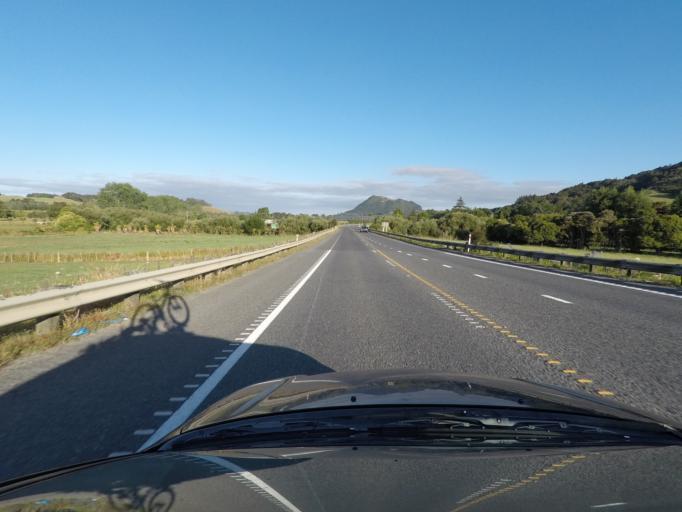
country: NZ
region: Northland
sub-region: Whangarei
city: Whangarei
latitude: -35.6263
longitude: 174.2943
